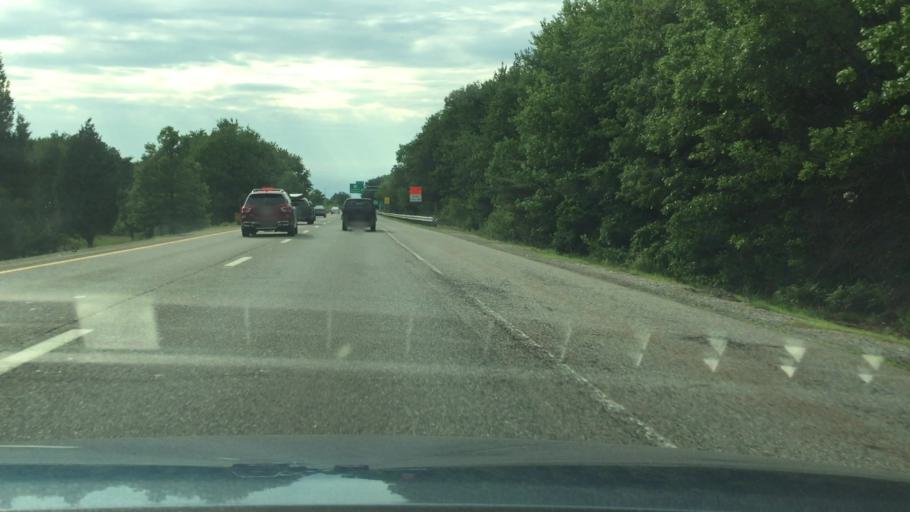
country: US
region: Massachusetts
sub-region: Plymouth County
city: Rockland
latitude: 42.1633
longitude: -70.8853
